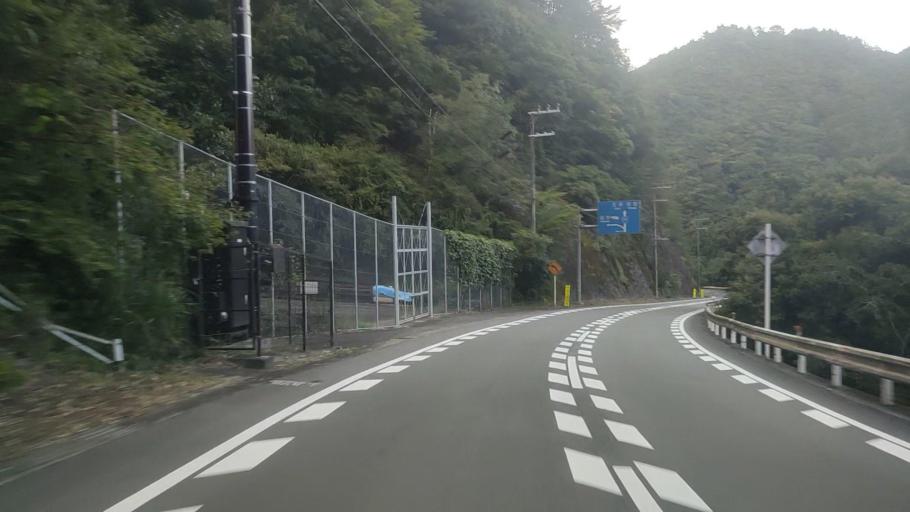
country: JP
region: Wakayama
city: Shingu
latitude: 33.8080
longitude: 135.7192
